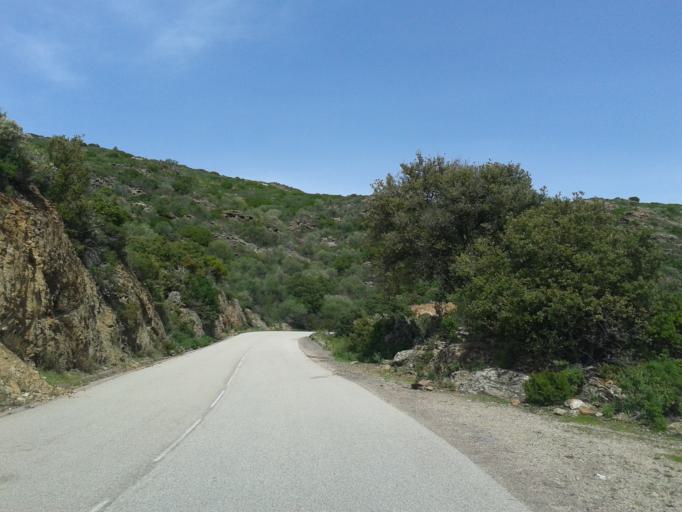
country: FR
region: Corsica
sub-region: Departement de la Haute-Corse
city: Monticello
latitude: 42.6584
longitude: 9.1219
